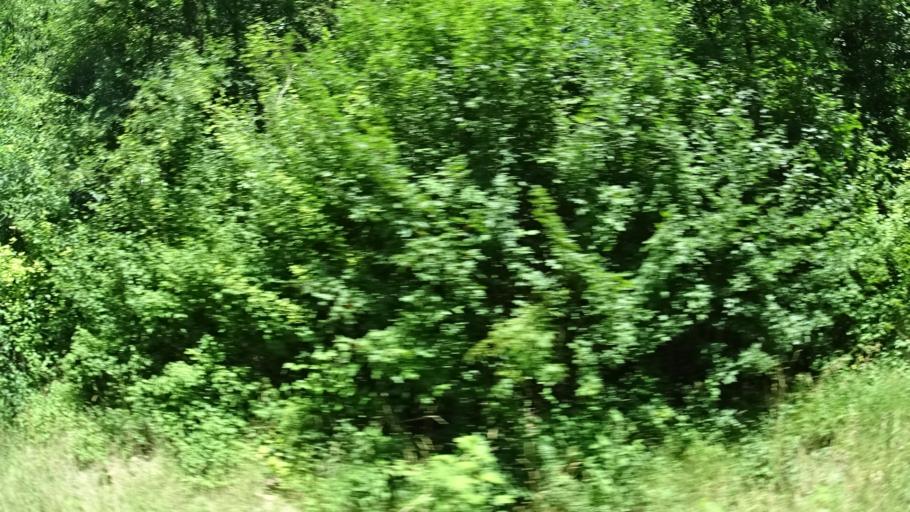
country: DE
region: Bavaria
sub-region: Regierungsbezirk Unterfranken
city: Guntersleben
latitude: 49.8722
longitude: 9.9214
